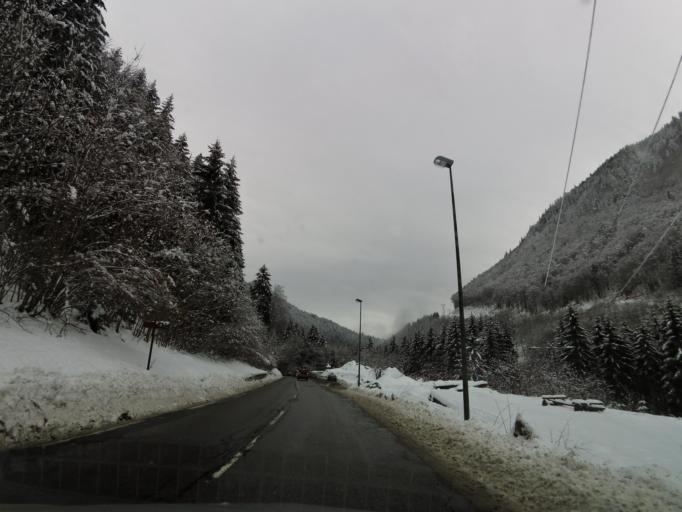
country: FR
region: Rhone-Alpes
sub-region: Departement de la Haute-Savoie
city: Taninges
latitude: 46.1323
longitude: 6.6245
